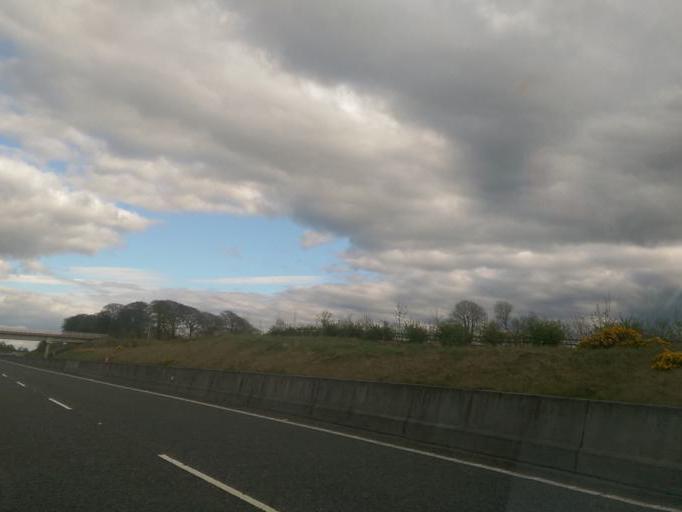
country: IE
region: Leinster
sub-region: Uibh Fhaili
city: Clara
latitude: 53.3849
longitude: -7.5864
